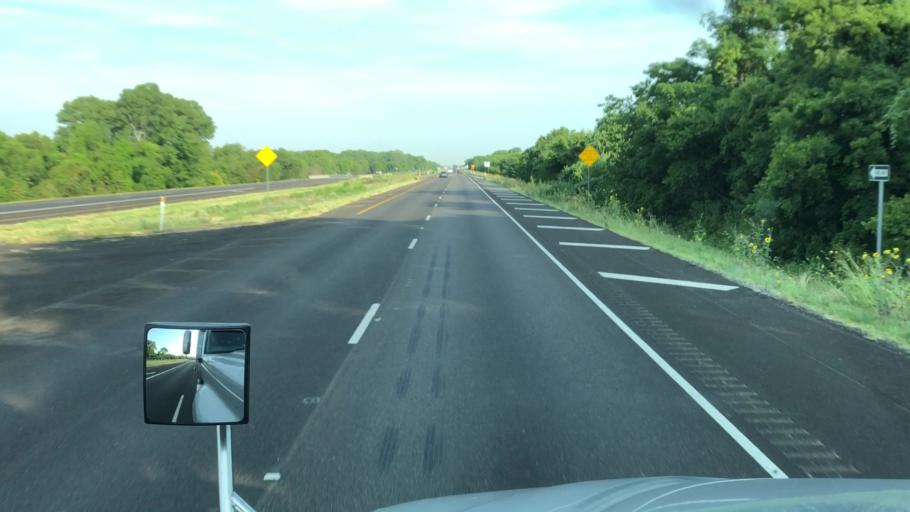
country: US
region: Texas
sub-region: McLennan County
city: Bellmead
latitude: 31.5380
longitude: -97.0384
